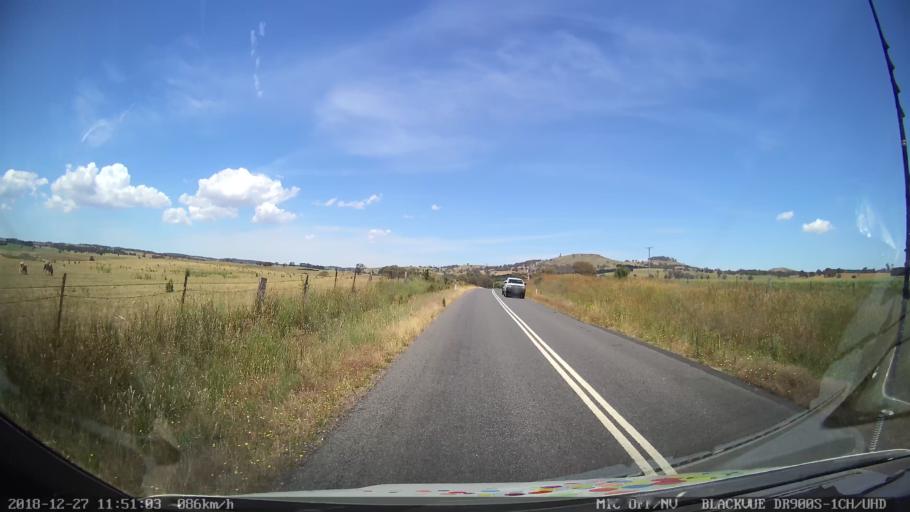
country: AU
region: New South Wales
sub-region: Bathurst Regional
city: Perthville
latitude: -33.6379
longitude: 149.4237
